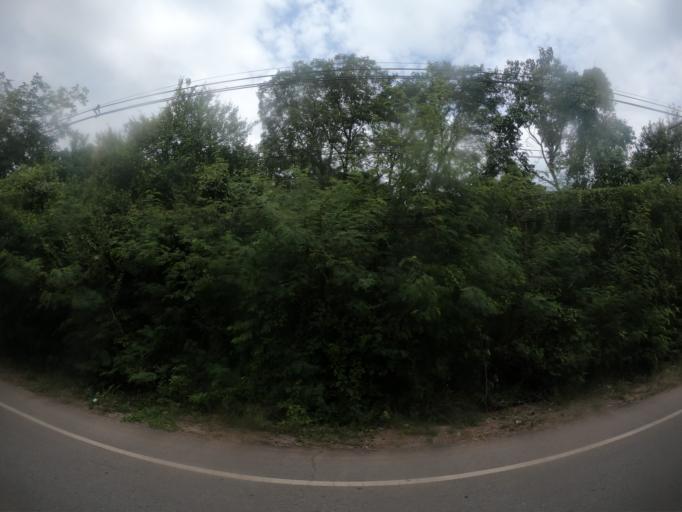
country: TH
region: Maha Sarakham
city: Kantharawichai
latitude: 16.3277
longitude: 103.2865
